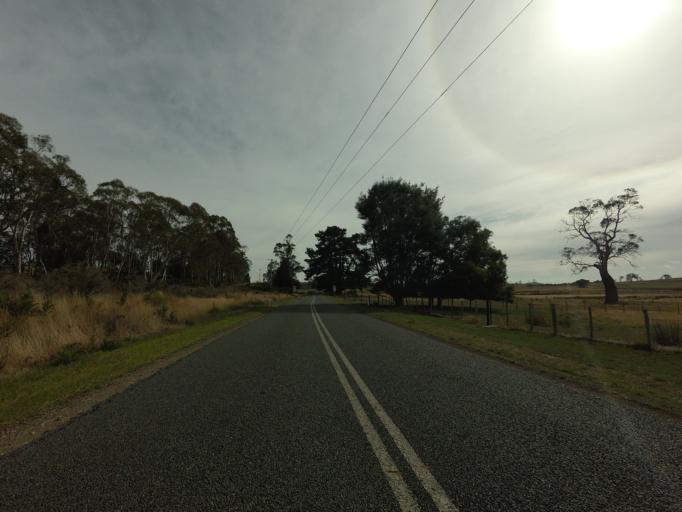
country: AU
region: Tasmania
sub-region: Brighton
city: Bridgewater
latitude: -42.3464
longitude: 147.4044
